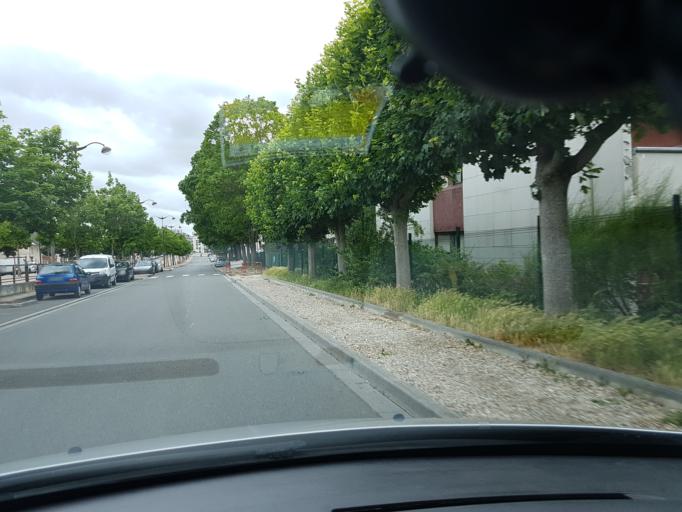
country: FR
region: Centre
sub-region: Departement du Cher
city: Bourges
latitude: 47.1063
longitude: 2.4087
